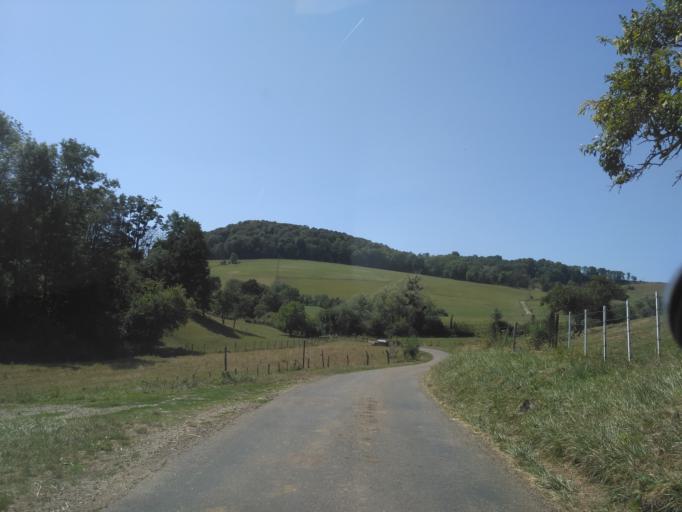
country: FR
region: Franche-Comte
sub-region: Departement de la Haute-Saone
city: Villersexel
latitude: 47.5106
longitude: 6.5160
